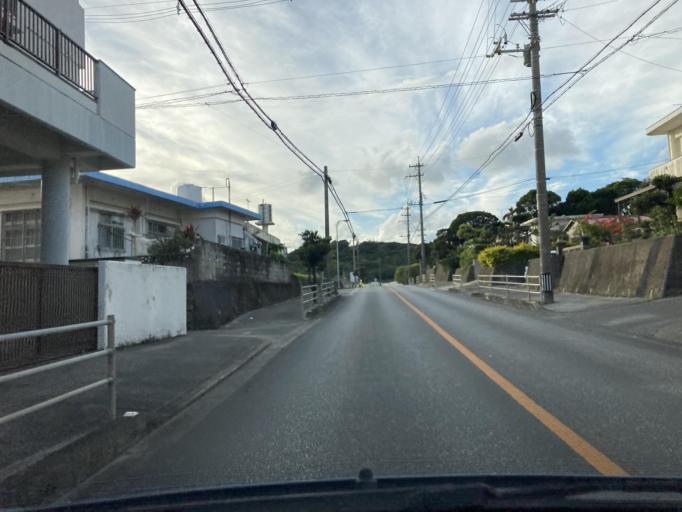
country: JP
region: Okinawa
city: Tomigusuku
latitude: 26.1508
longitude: 127.7063
